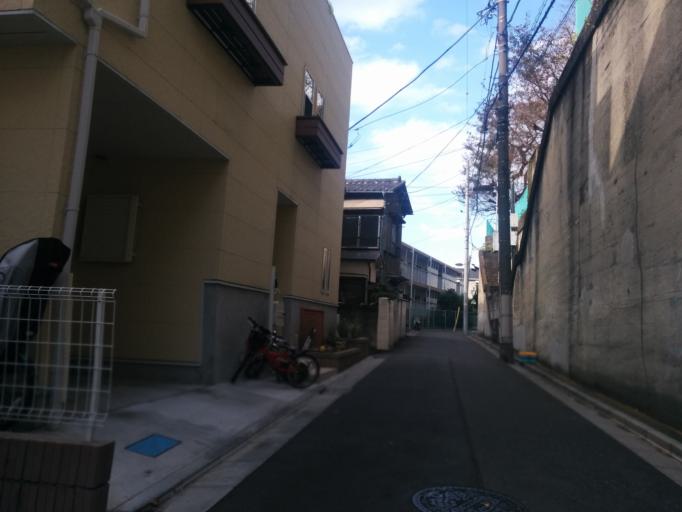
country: JP
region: Tokyo
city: Tokyo
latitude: 35.7175
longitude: 139.7535
